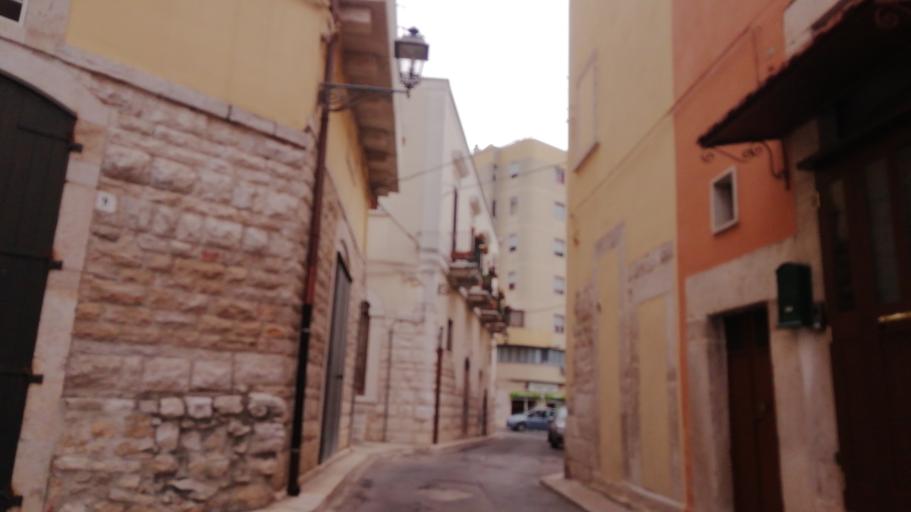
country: IT
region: Apulia
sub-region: Provincia di Barletta - Andria - Trani
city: Andria
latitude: 41.2243
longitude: 16.2979
